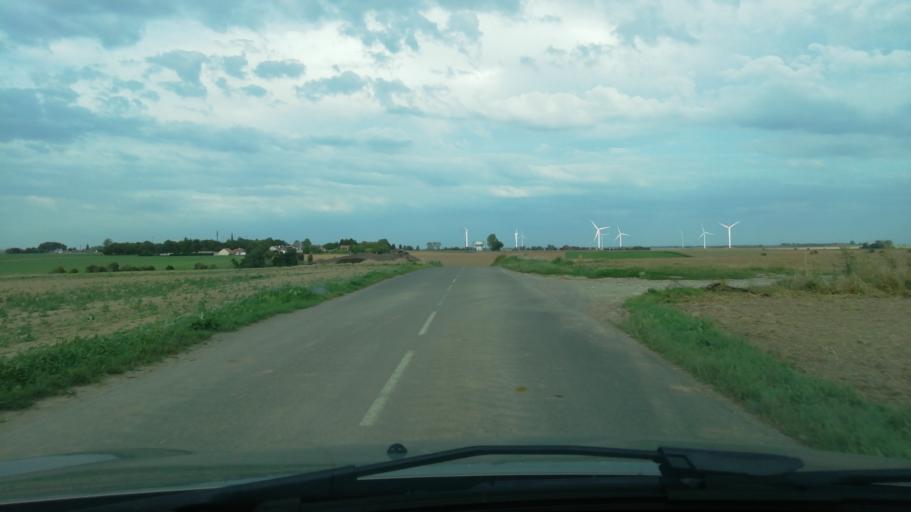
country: FR
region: Nord-Pas-de-Calais
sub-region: Departement du Nord
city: Saint-Hilaire-lez-Cambrai
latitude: 50.1753
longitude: 3.3976
